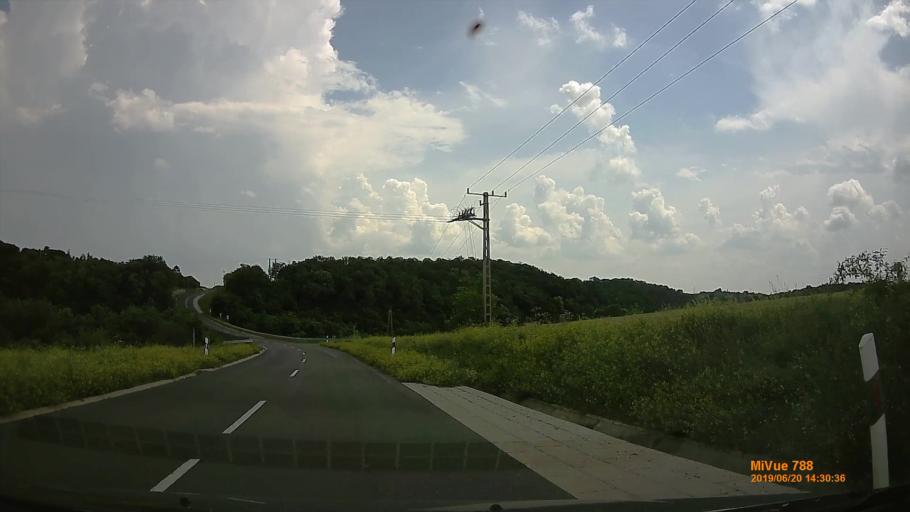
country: HU
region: Baranya
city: Hosszuheteny
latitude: 46.1475
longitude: 18.3460
